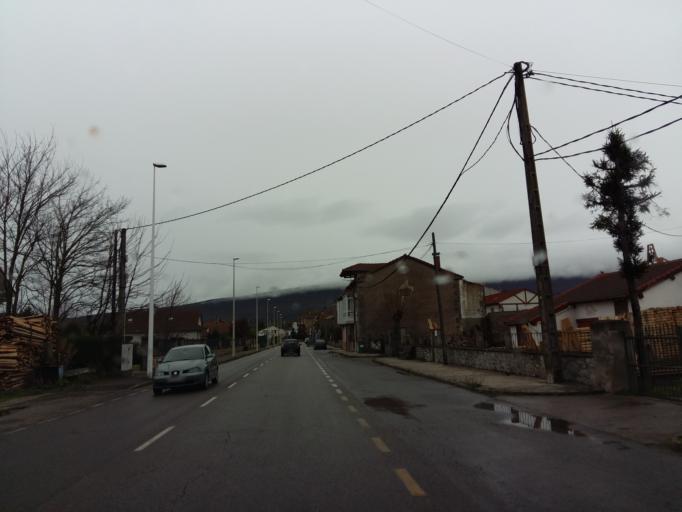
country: ES
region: Cantabria
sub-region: Provincia de Cantabria
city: Reinosa
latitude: 42.9836
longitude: -4.1477
